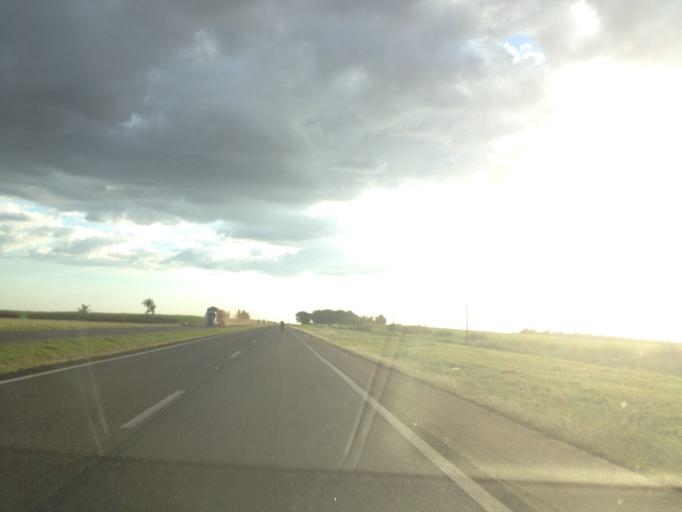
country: BR
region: Sao Paulo
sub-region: Jau
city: Jau
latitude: -22.2695
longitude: -48.4624
